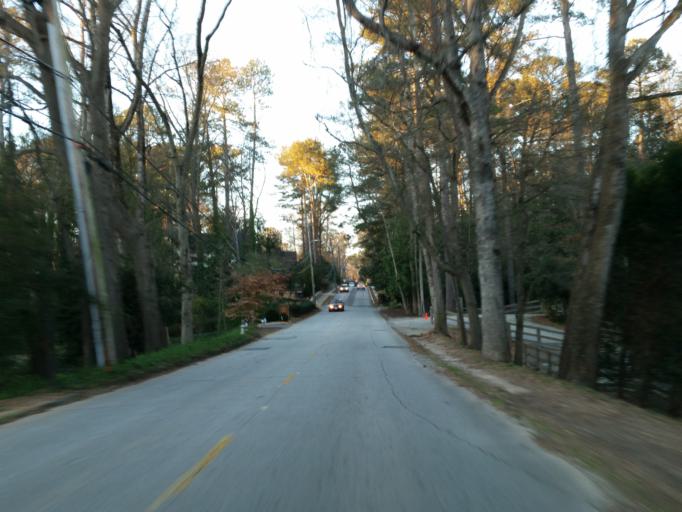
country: US
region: Georgia
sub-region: Cobb County
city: Vinings
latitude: 33.8237
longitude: -84.4292
